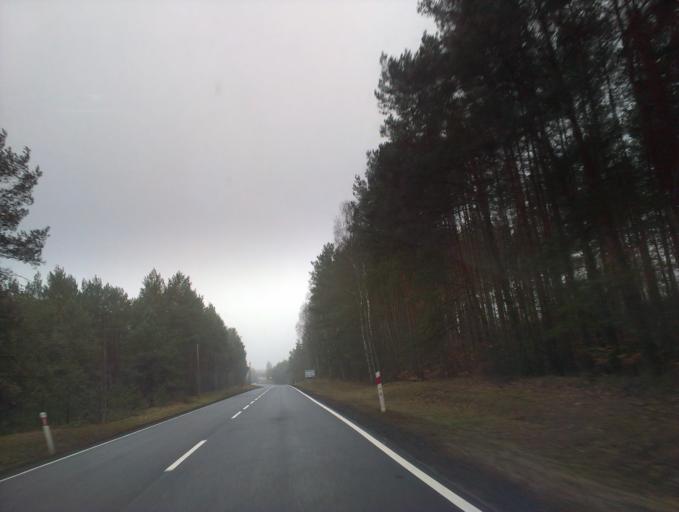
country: PL
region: Greater Poland Voivodeship
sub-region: Powiat zlotowski
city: Tarnowka
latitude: 53.3139
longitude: 16.7940
